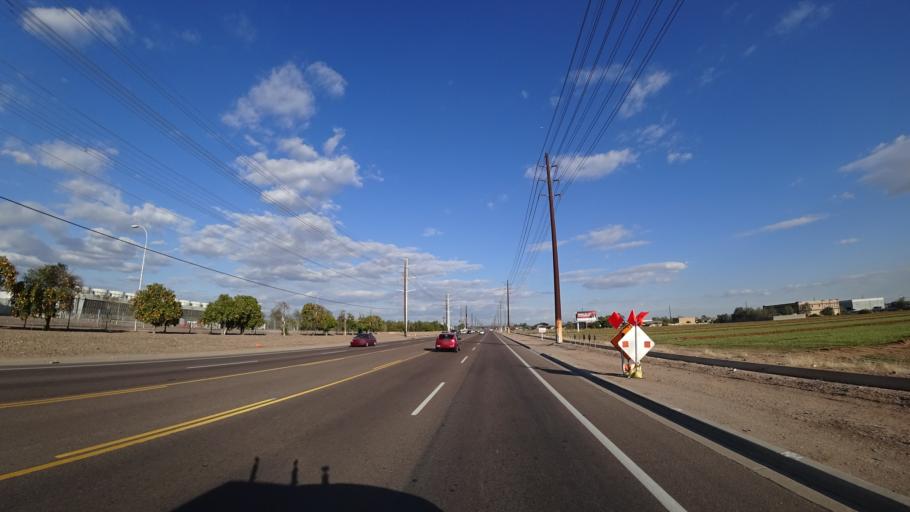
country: US
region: Arizona
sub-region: Maricopa County
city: Glendale
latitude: 33.5525
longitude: -112.2152
